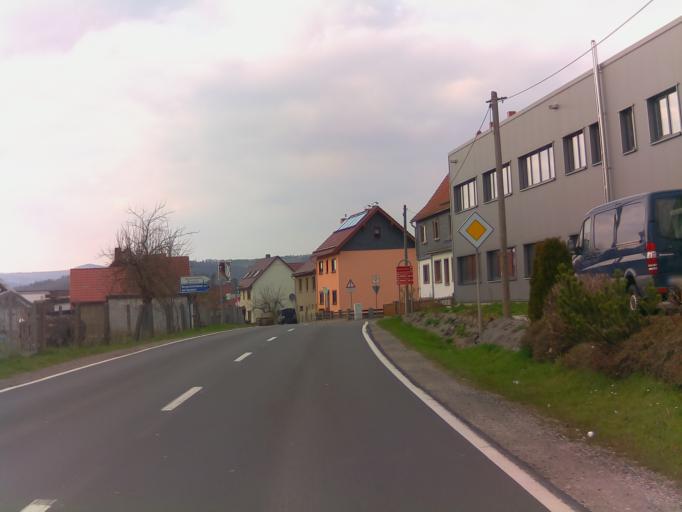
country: DE
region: Thuringia
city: Altersbach
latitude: 50.7397
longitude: 10.5118
